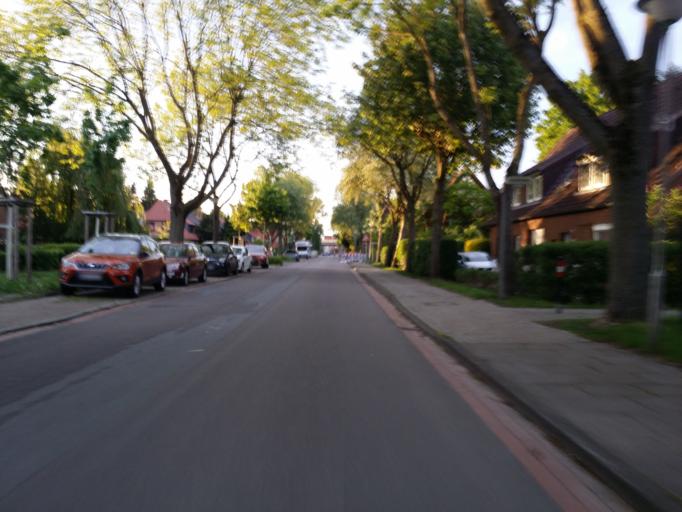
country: DE
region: Lower Saxony
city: Stuhr
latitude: 53.0572
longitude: 8.7644
